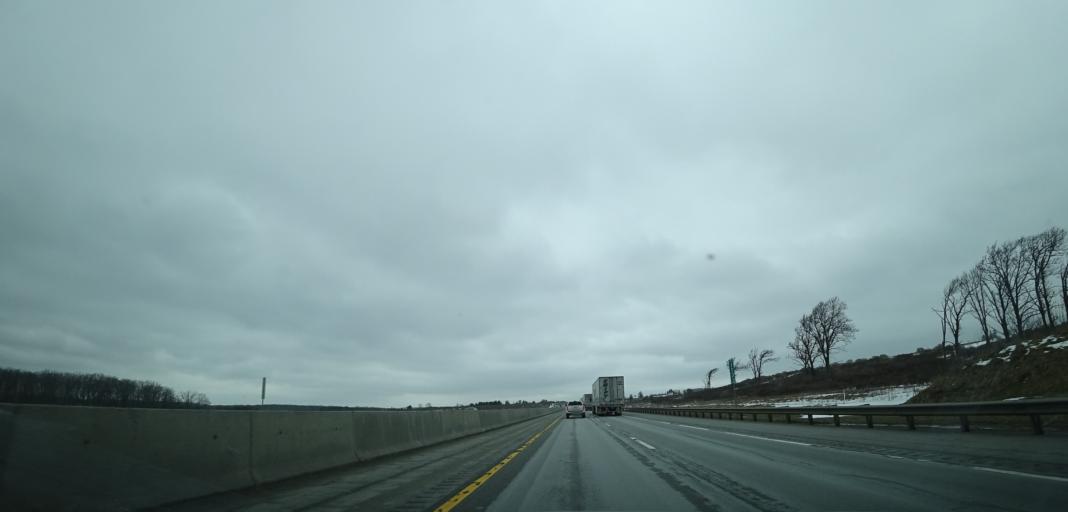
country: US
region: Pennsylvania
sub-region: Somerset County
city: Somerset
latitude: 39.9952
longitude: -79.0307
